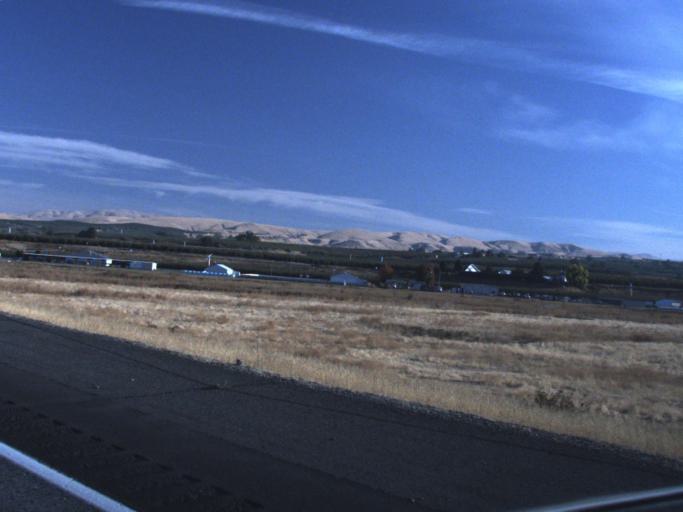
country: US
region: Washington
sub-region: Yakima County
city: Toppenish
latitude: 46.4402
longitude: -120.3451
